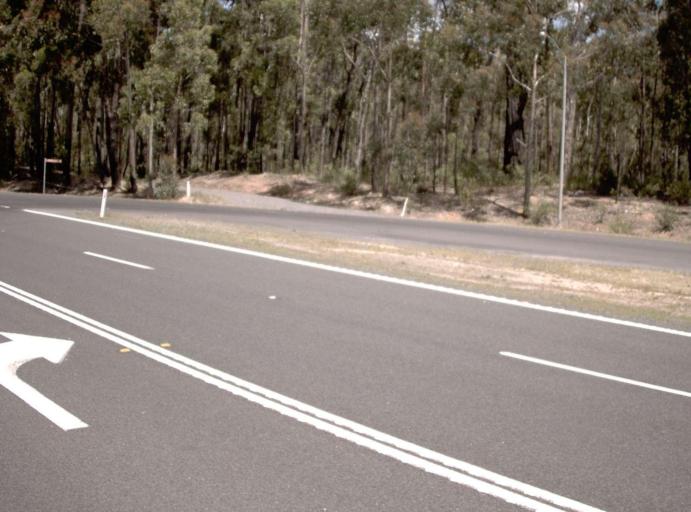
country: AU
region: New South Wales
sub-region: Bombala
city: Bombala
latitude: -37.5668
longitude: 149.1085
